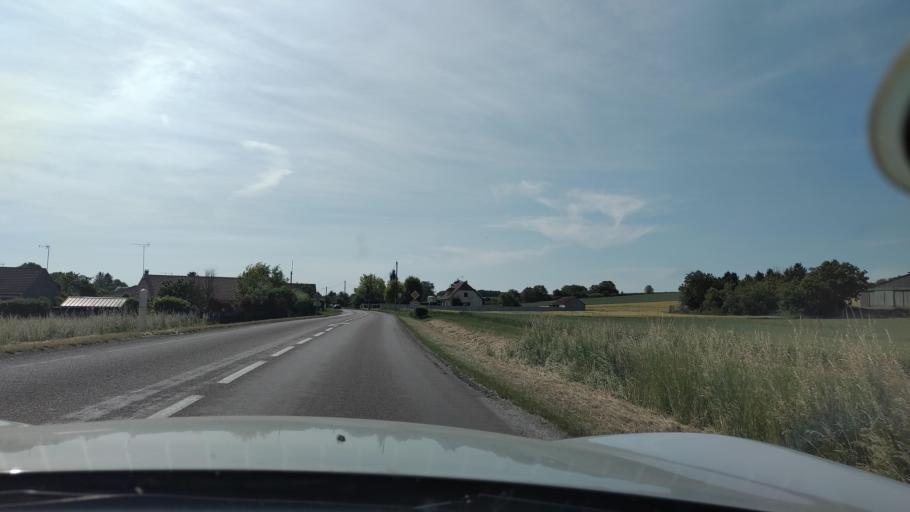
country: FR
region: Champagne-Ardenne
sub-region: Departement de l'Aube
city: Marigny-le-Chatel
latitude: 48.4426
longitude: 3.6467
